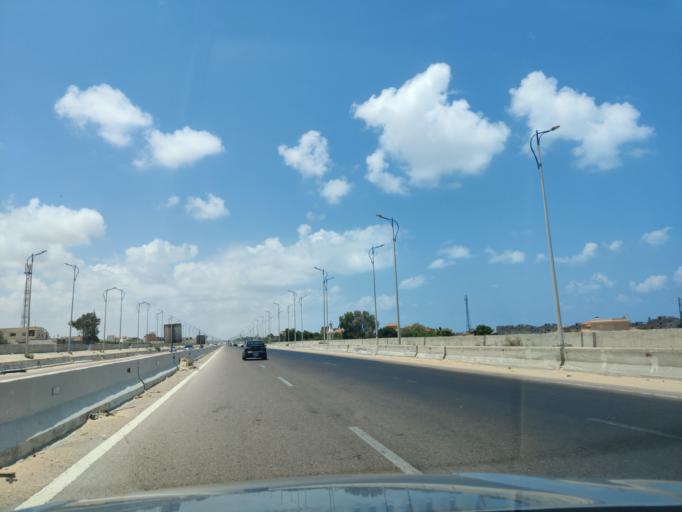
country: EG
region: Alexandria
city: Alexandria
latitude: 30.9590
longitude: 29.5394
